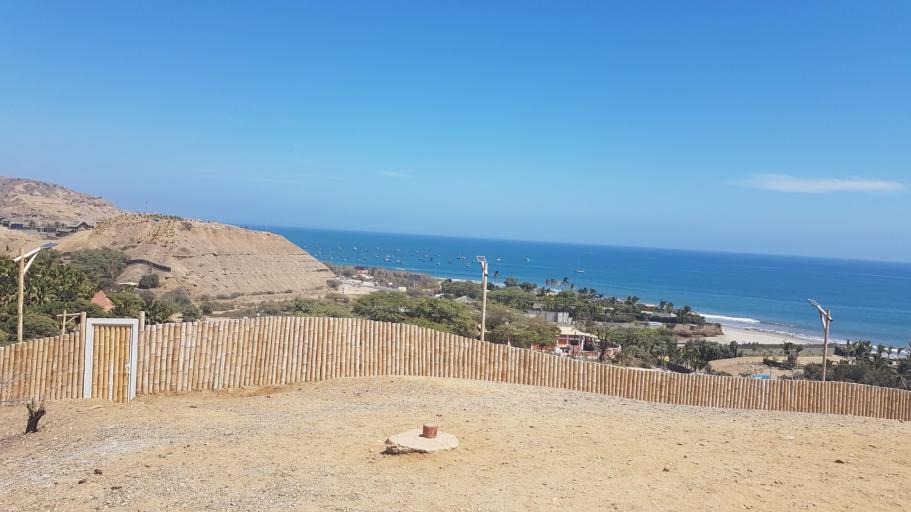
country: PE
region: Piura
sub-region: Provincia de Talara
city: Mancora
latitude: -4.1090
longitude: -81.0578
